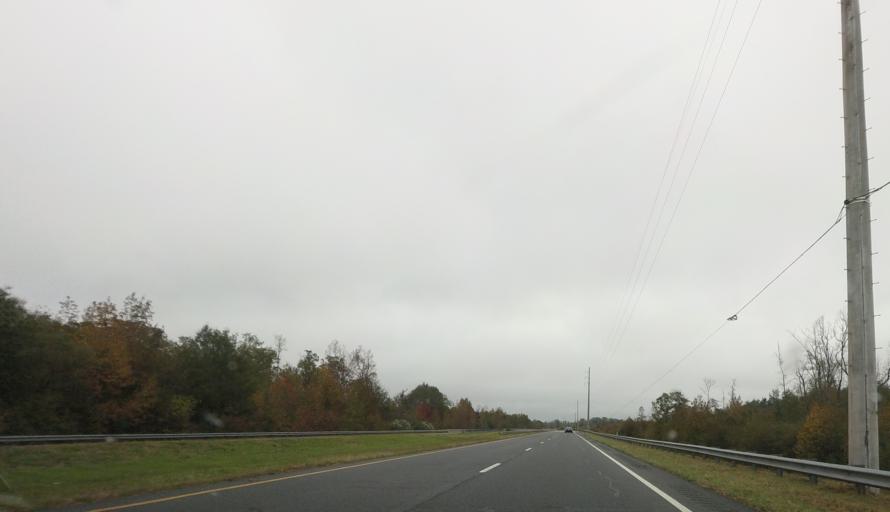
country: US
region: Georgia
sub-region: Taylor County
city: Reynolds
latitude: 32.5439
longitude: -84.0331
